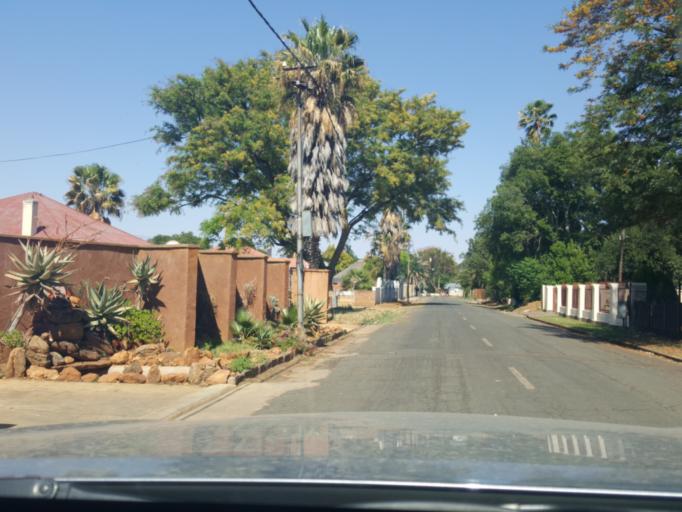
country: ZA
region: North-West
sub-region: Ngaka Modiri Molema District Municipality
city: Zeerust
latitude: -25.5429
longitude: 26.0760
